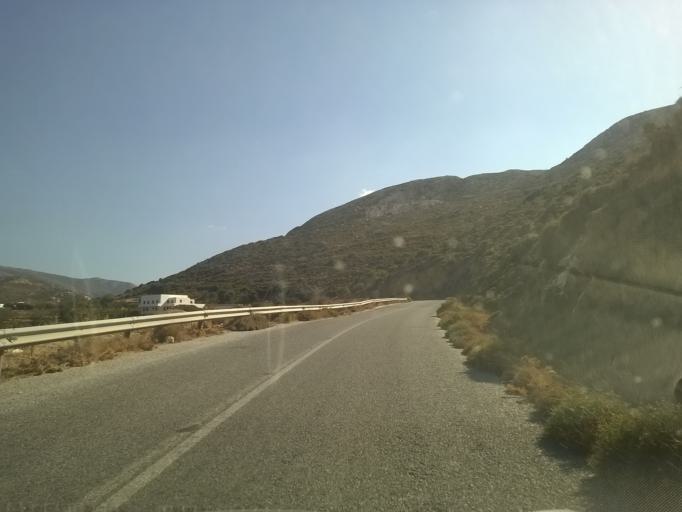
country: GR
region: South Aegean
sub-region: Nomos Kykladon
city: Filotion
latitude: 37.0960
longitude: 25.4689
